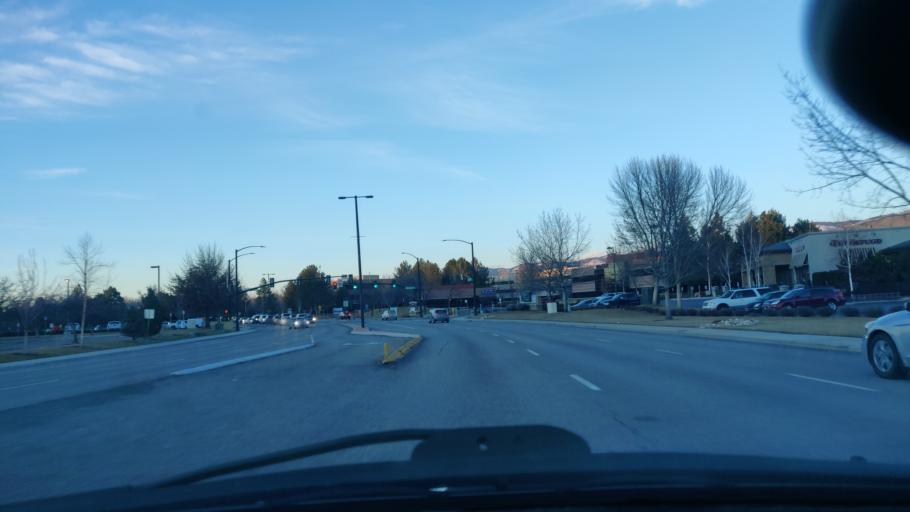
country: US
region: Idaho
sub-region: Ada County
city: Boise
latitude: 43.5956
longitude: -116.1778
